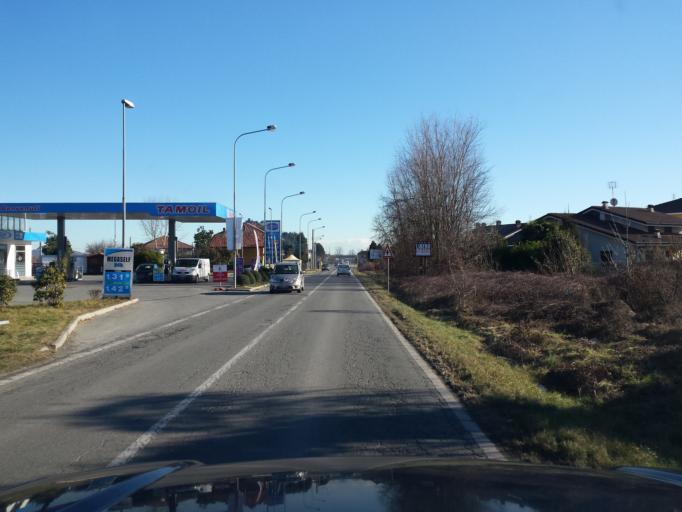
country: IT
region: Piedmont
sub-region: Provincia di Torino
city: Castellamonte
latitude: 45.3692
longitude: 7.7186
